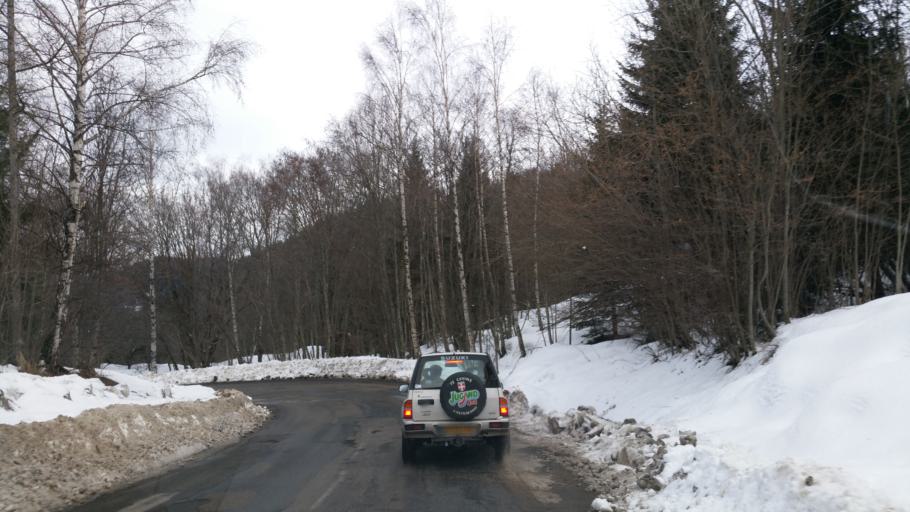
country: FR
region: Rhone-Alpes
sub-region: Departement de la Savoie
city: Saint-Jean-de-Maurienne
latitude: 45.2671
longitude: 6.3025
